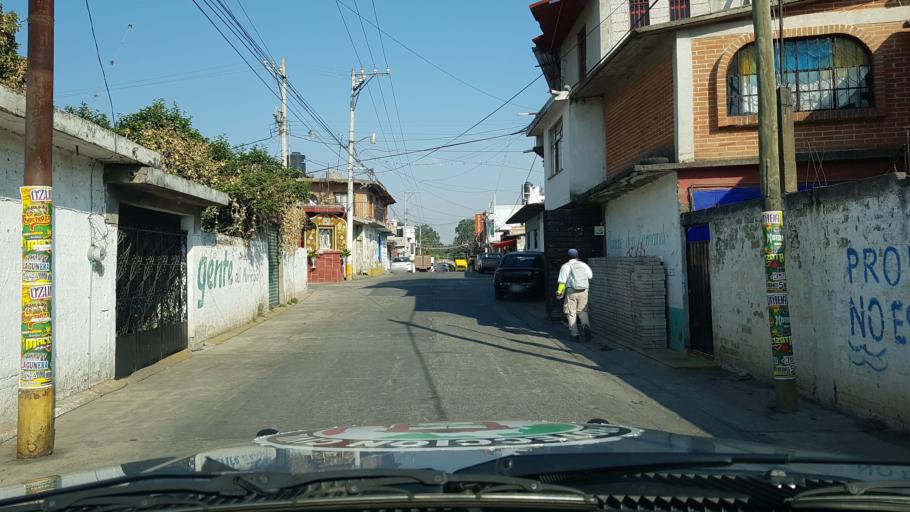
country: MX
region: Mexico
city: Ozumba de Alzate
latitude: 19.0562
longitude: -98.7734
